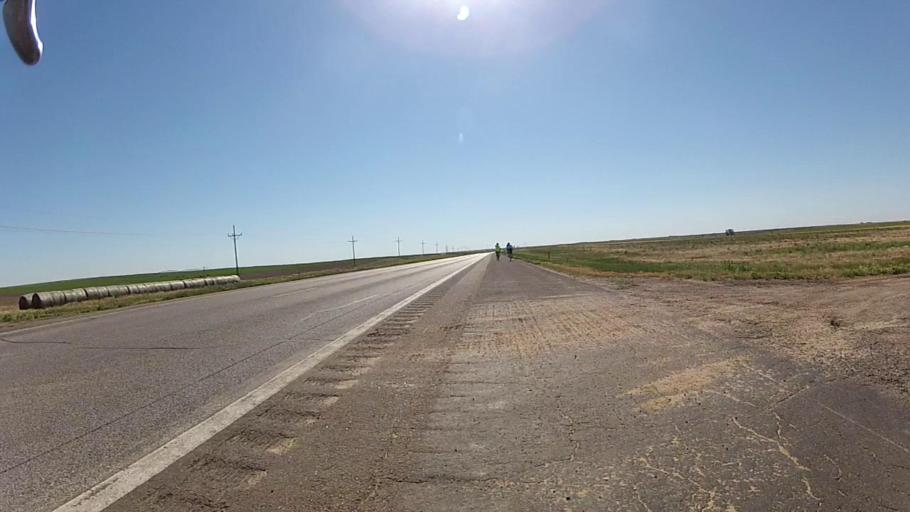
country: US
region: Kansas
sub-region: Kiowa County
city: Greensburg
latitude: 37.5864
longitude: -99.5667
